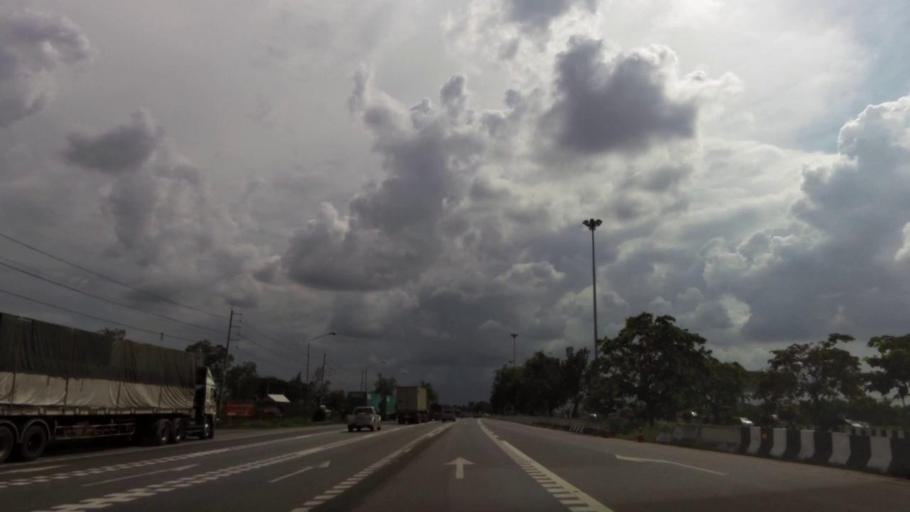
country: TH
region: Phra Nakhon Si Ayutthaya
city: Bang Pa-in
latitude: 14.2047
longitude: 100.6091
